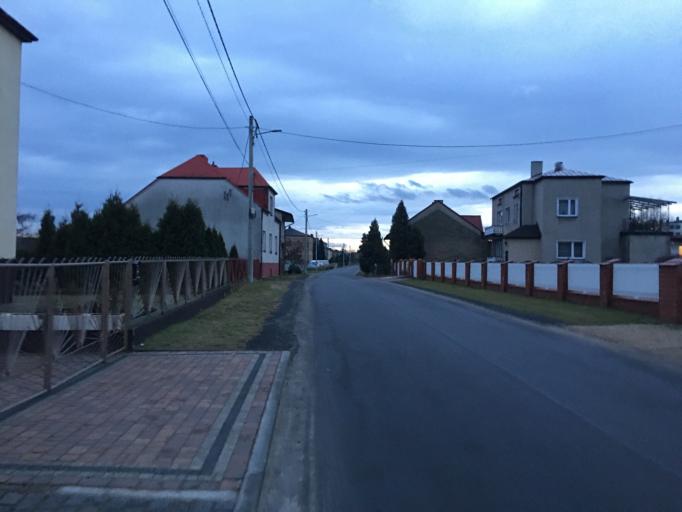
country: PL
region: Silesian Voivodeship
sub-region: Powiat myszkowski
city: Myszkow
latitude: 50.5436
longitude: 19.3696
